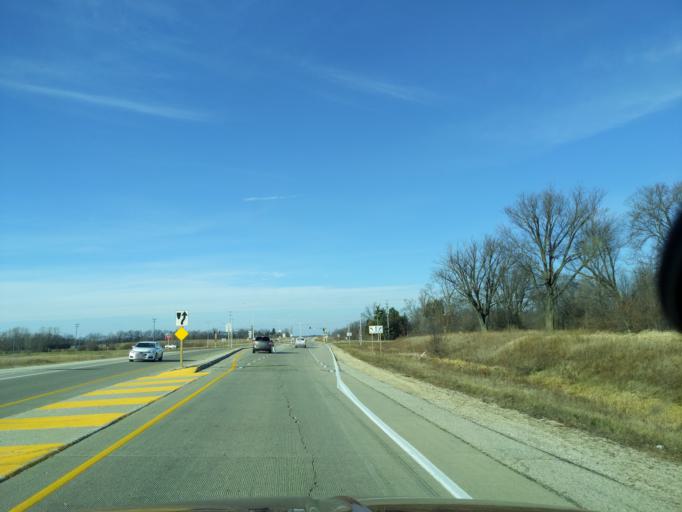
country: US
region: Wisconsin
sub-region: Walworth County
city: Whitewater
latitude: 42.8255
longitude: -88.7693
